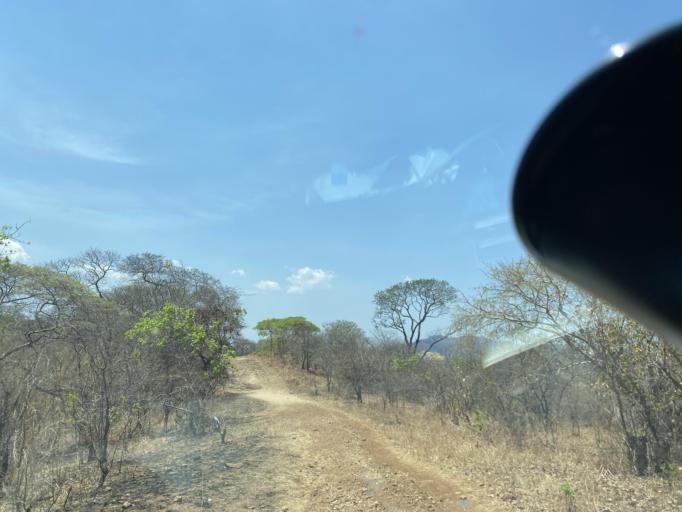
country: ZM
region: Lusaka
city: Kafue
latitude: -15.8005
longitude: 28.4554
